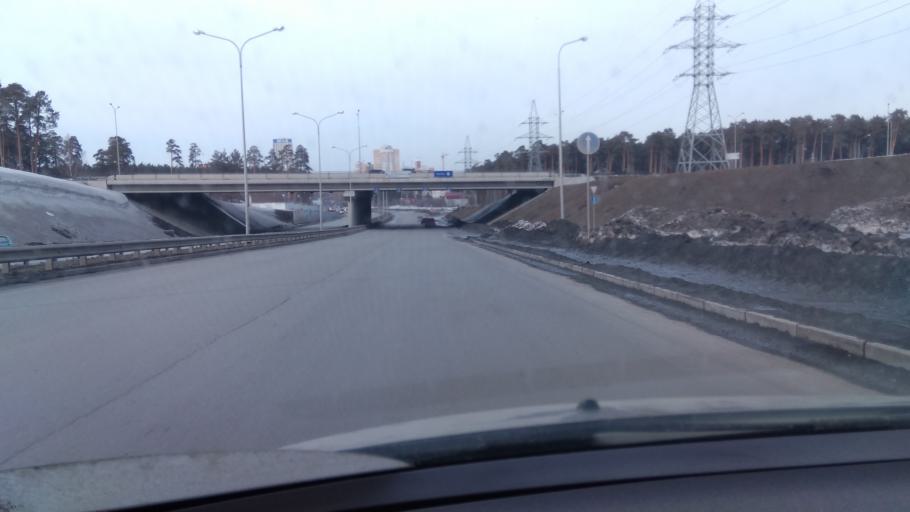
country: RU
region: Sverdlovsk
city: Sovkhoznyy
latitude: 56.7887
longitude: 60.5979
